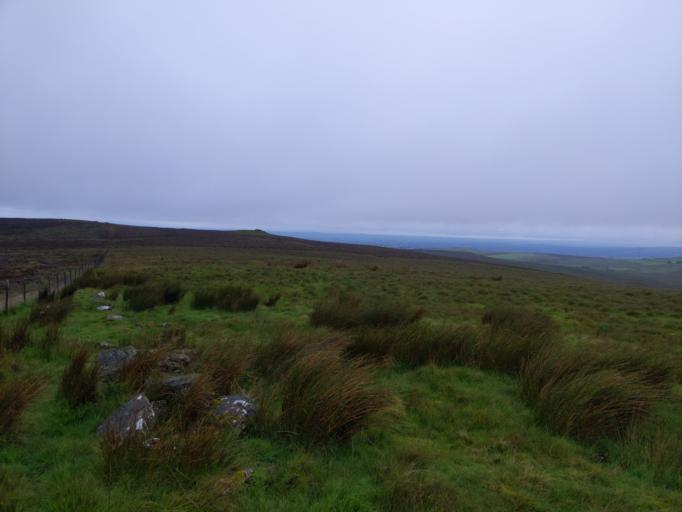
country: GB
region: Northern Ireland
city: Ballyclare
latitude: 54.8600
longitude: -6.0564
